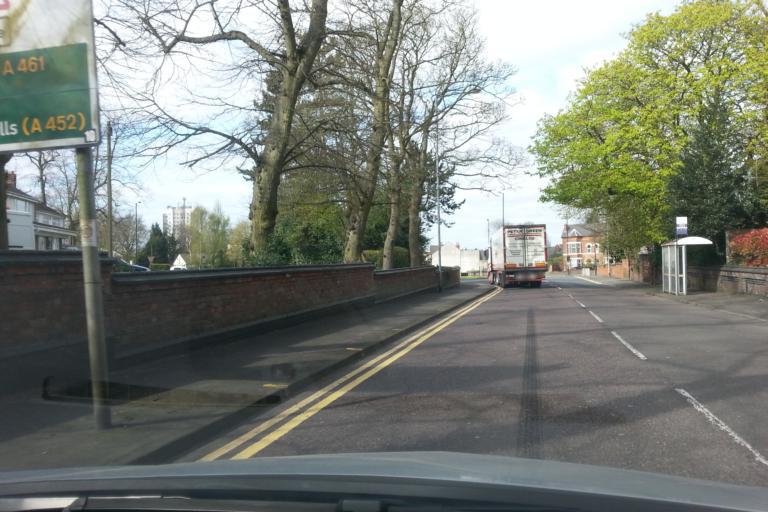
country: GB
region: England
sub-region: Walsall
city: Walsall
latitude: 52.5926
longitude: -1.9697
